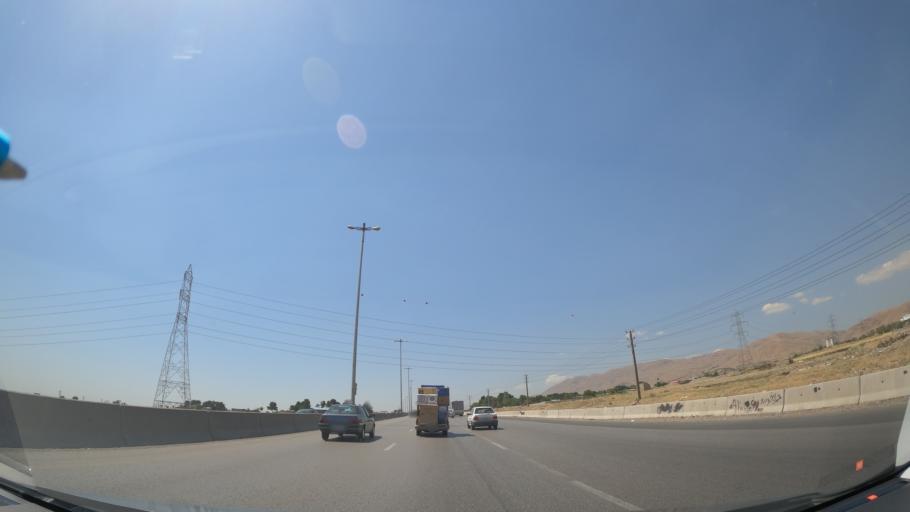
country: IR
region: Alborz
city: Karaj
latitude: 35.8704
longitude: 50.8979
